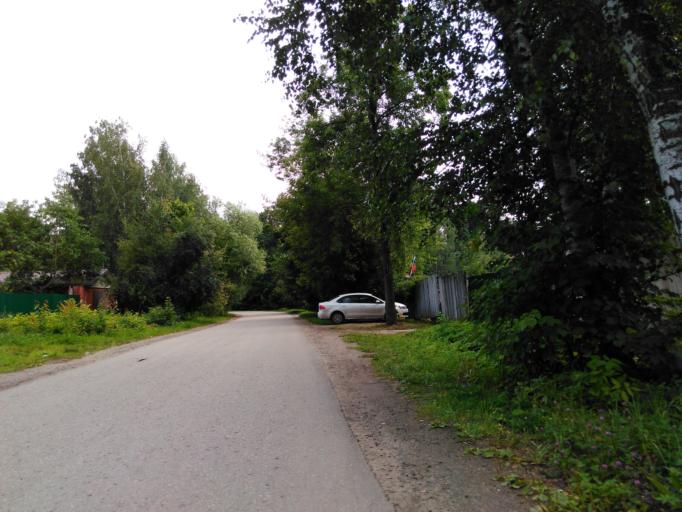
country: RU
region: Moskovskaya
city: Pravdinskiy
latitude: 56.0418
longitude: 37.8511
